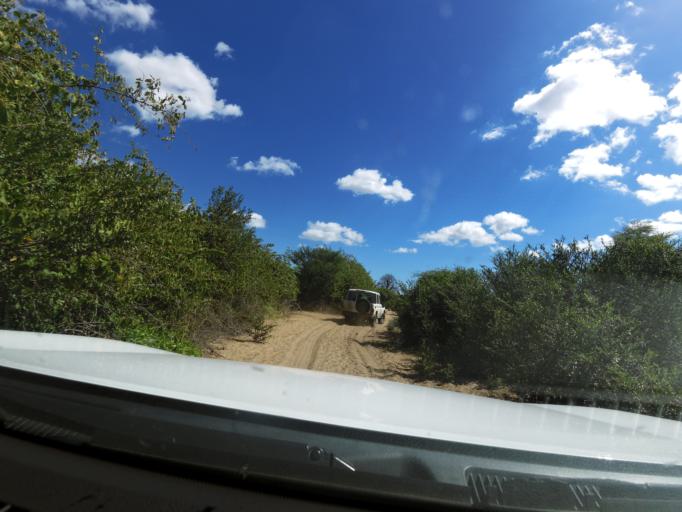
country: ZW
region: Matabeleland North
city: Kamativi Mine
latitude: -18.0058
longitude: 27.1453
